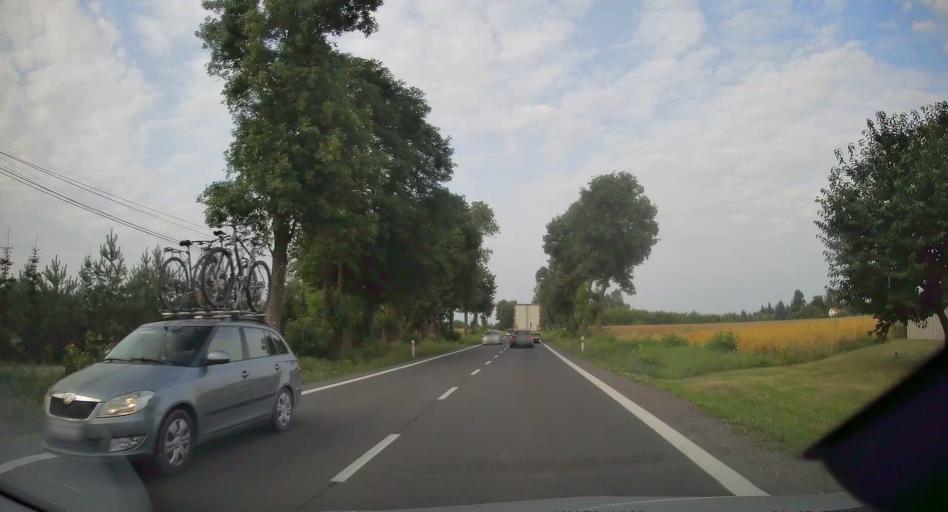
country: PL
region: Silesian Voivodeship
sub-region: Powiat czestochowski
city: Borowno
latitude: 50.9056
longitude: 19.2957
